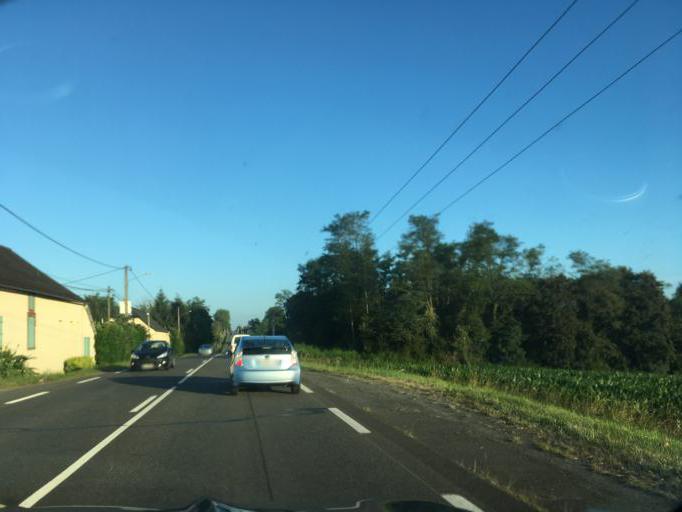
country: FR
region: Aquitaine
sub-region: Departement des Pyrenees-Atlantiques
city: Ger
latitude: 43.2455
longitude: -0.0317
